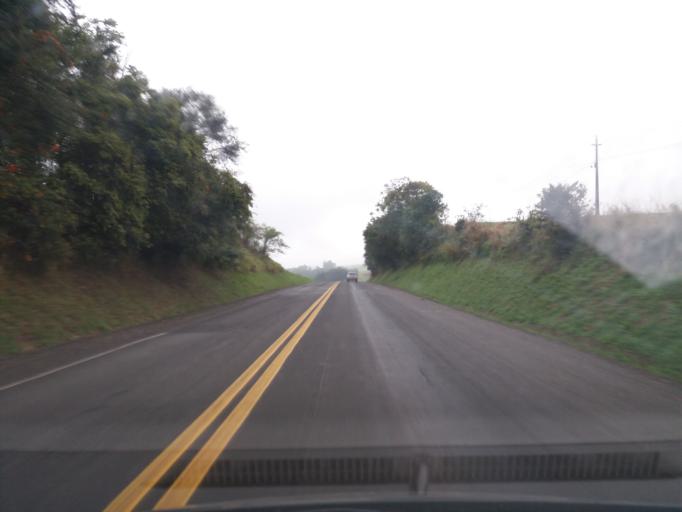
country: BR
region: Parana
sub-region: Realeza
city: Realeza
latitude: -25.8441
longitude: -53.5083
